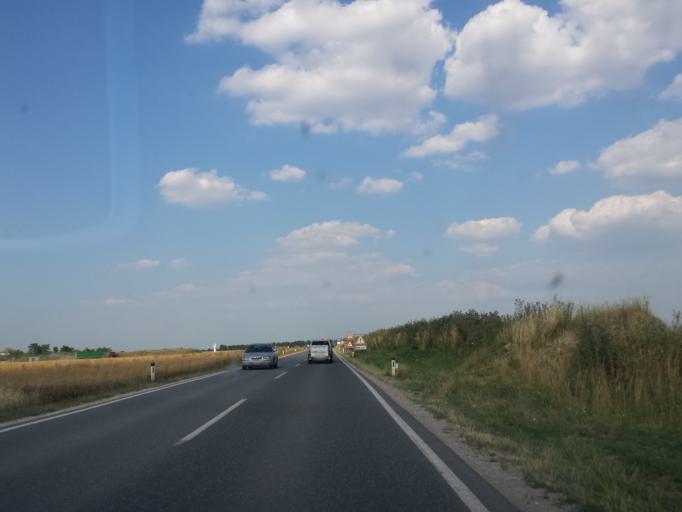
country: AT
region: Lower Austria
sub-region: Politischer Bezirk Ganserndorf
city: Untersiebenbrunn
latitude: 48.2569
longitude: 16.7619
